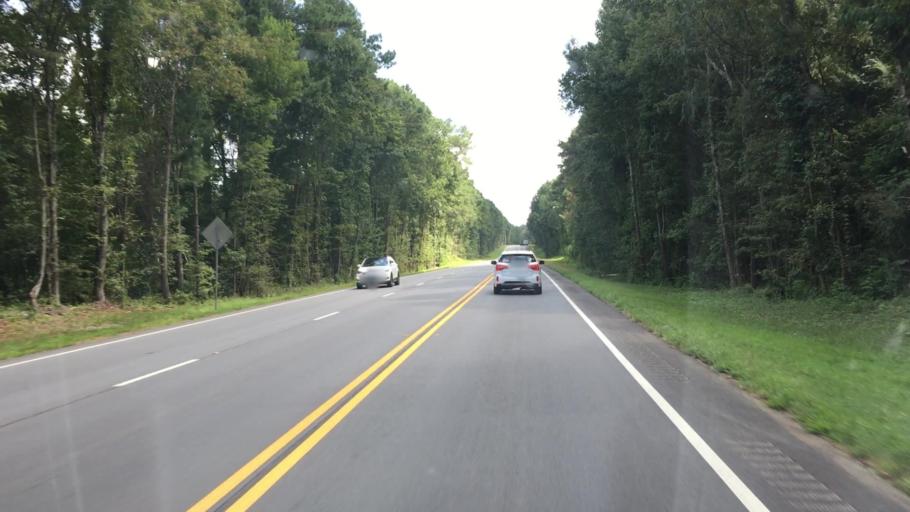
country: US
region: Georgia
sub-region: Putnam County
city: Jefferson
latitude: 33.4327
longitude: -83.3748
